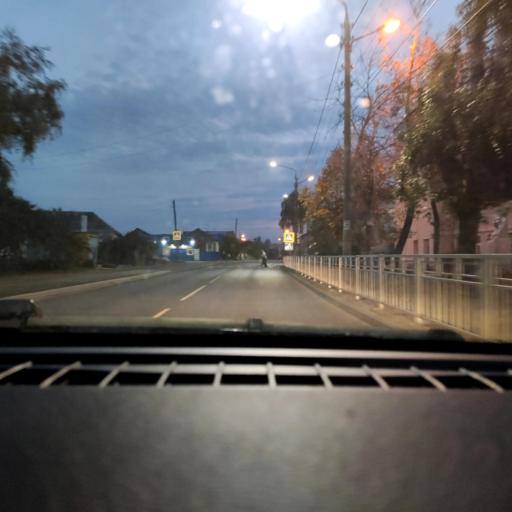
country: RU
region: Voronezj
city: Somovo
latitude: 51.7346
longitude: 39.2668
